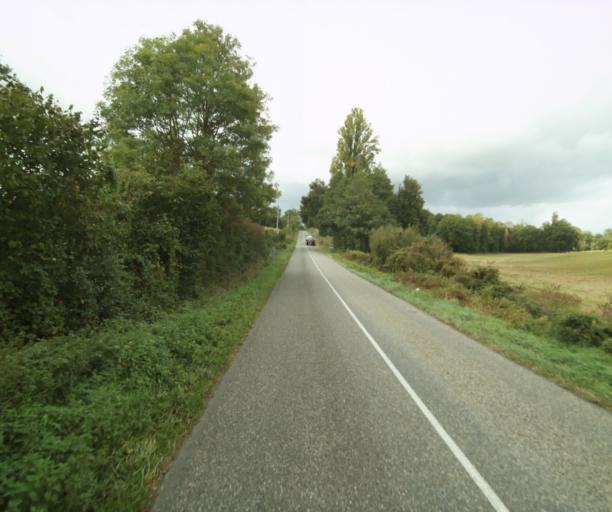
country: FR
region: Midi-Pyrenees
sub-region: Departement du Gers
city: Eauze
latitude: 43.8593
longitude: 0.0406
